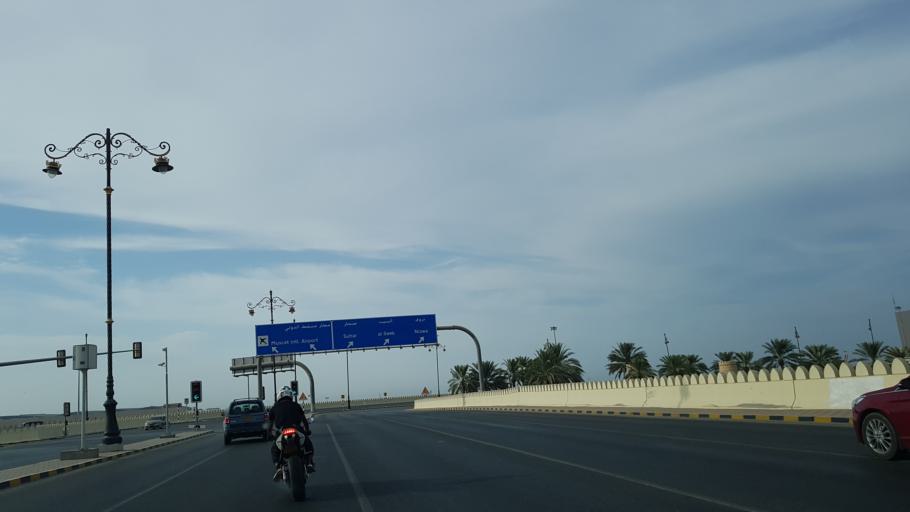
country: OM
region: Muhafazat Masqat
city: Bawshar
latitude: 23.5864
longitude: 58.2958
